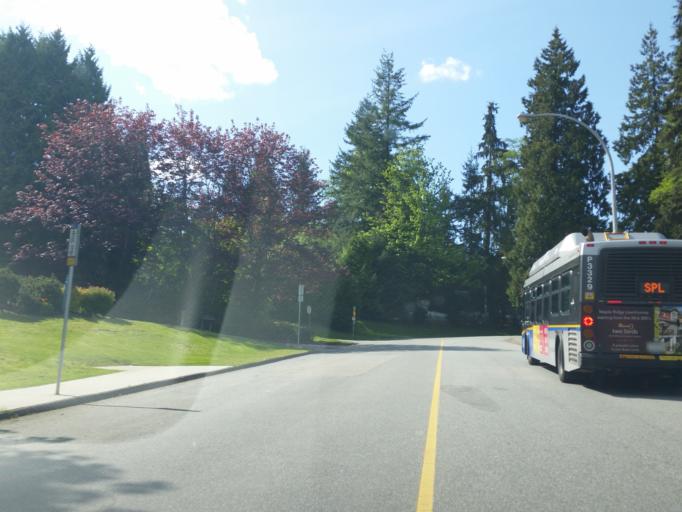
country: CA
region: British Columbia
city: Port Moody
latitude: 49.2758
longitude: -122.8746
